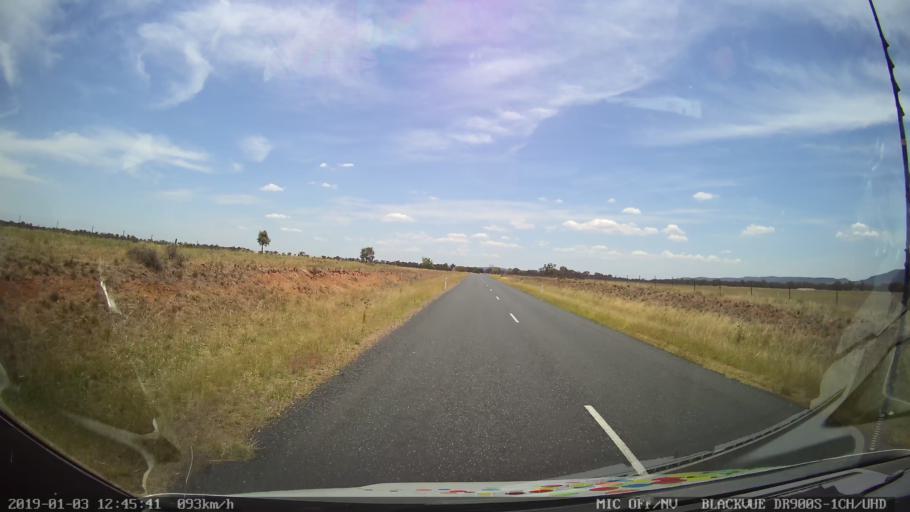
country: AU
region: New South Wales
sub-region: Weddin
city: Grenfell
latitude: -33.7462
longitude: 148.2255
